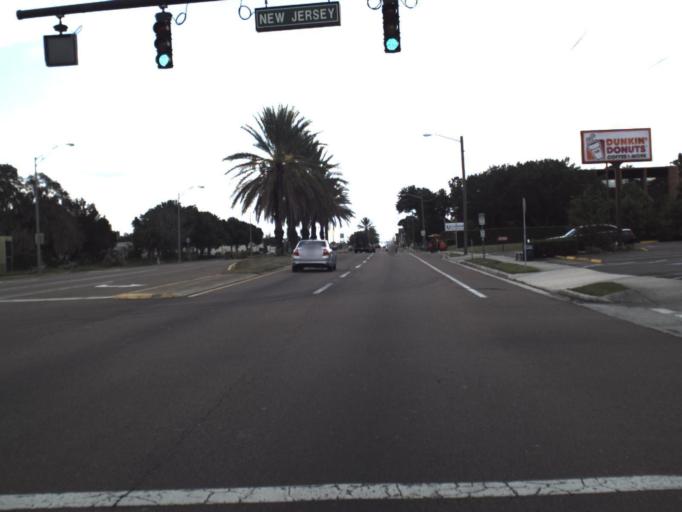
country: US
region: Florida
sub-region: Polk County
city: Lakeland
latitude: 28.0305
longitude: -81.9322
